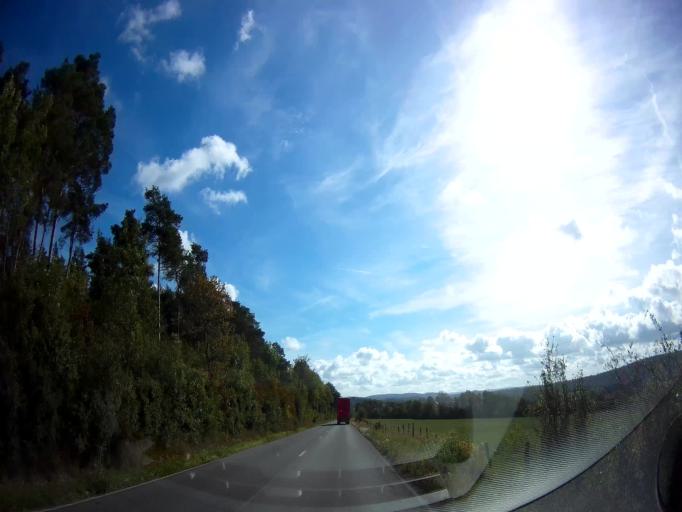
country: BE
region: Wallonia
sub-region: Province de Namur
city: Rochefort
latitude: 50.1673
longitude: 5.1825
